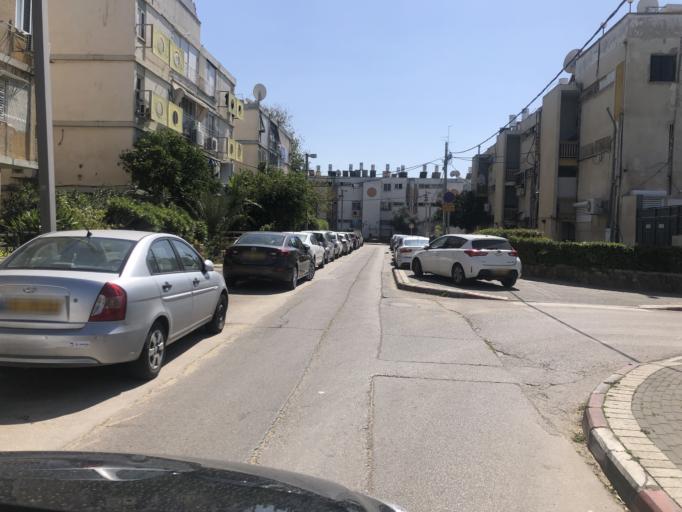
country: IL
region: Tel Aviv
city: Holon
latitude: 32.0024
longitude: 34.7625
